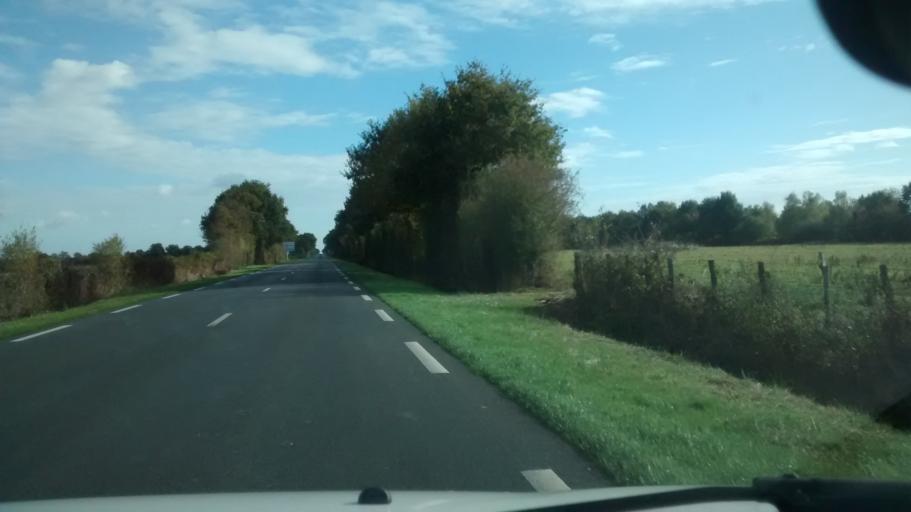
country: FR
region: Pays de la Loire
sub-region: Departement de la Loire-Atlantique
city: Soudan
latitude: 47.7447
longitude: -1.2484
